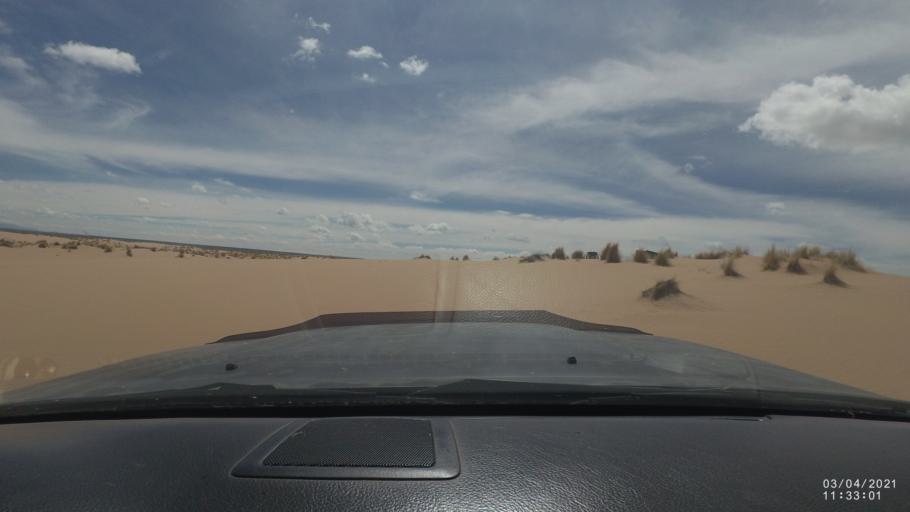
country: BO
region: Oruro
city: Poopo
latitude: -18.7019
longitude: -67.5058
